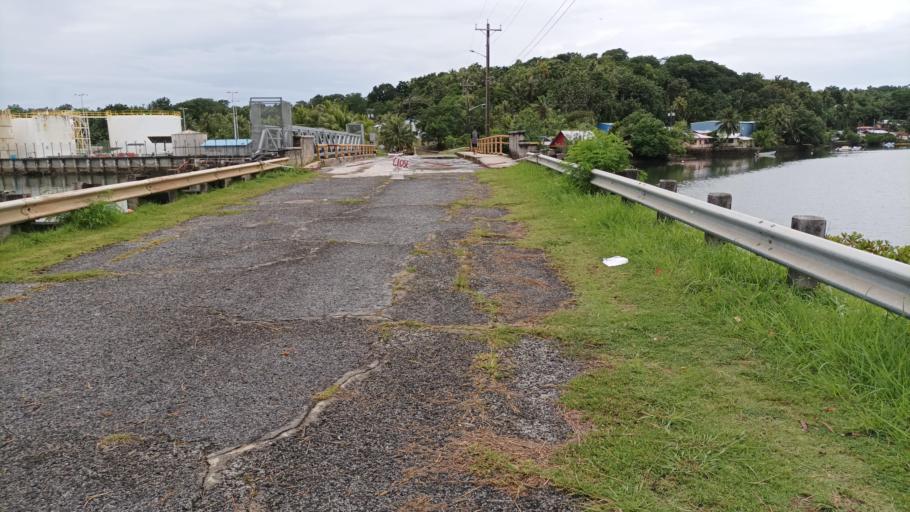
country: FM
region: Yap
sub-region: Weloy Municipality
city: Colonia
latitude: 9.5157
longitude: 138.1216
